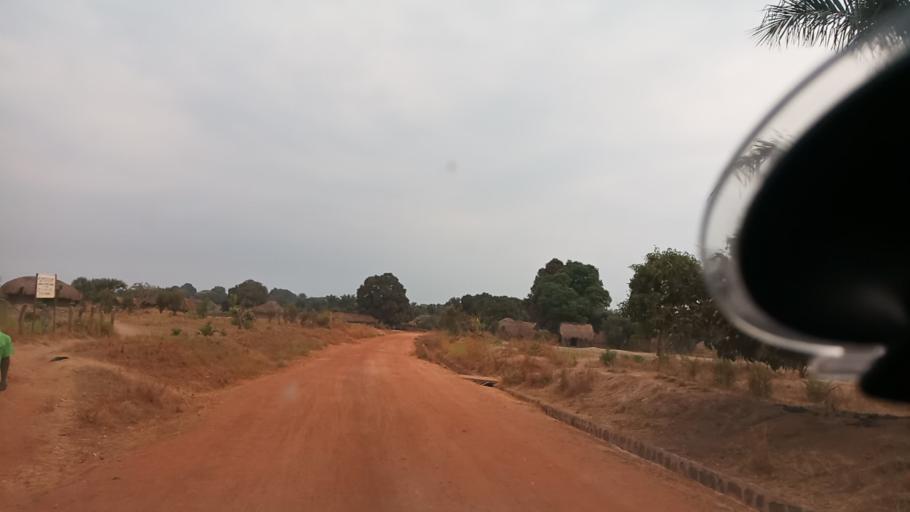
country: ZM
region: Luapula
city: Nchelenge
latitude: -9.1051
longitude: 28.3010
